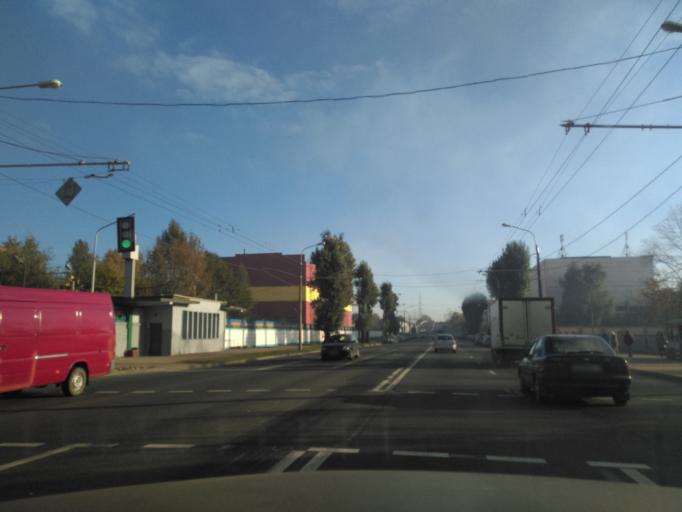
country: BY
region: Minsk
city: Minsk
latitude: 53.8888
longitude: 27.6305
